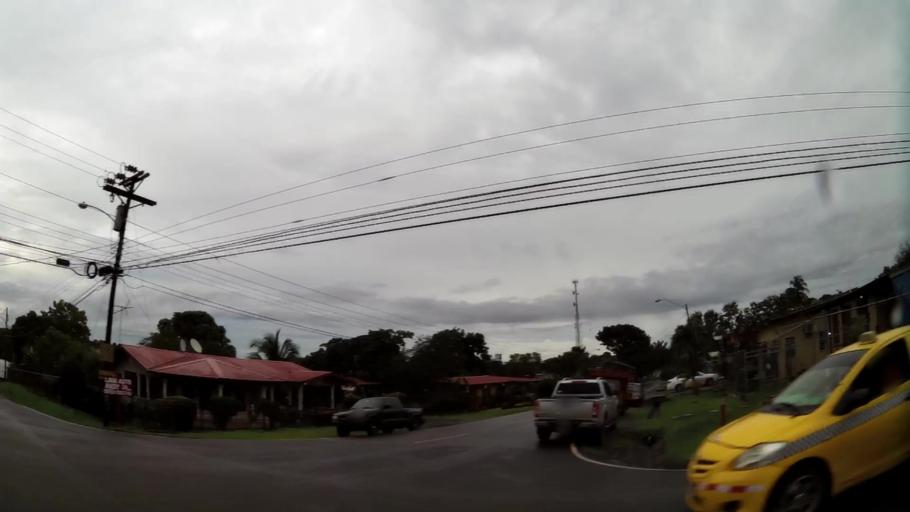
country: PA
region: Veraguas
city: Santiago de Veraguas
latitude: 8.1105
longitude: -80.9763
